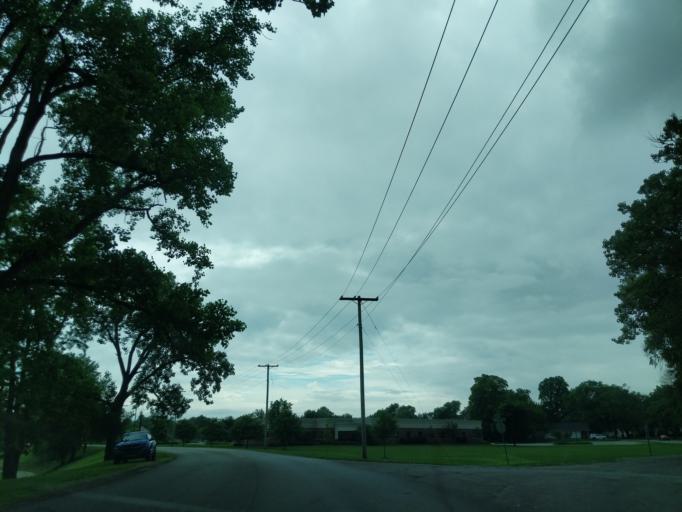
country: US
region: Indiana
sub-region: Delaware County
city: Muncie
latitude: 40.1952
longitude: -85.3966
